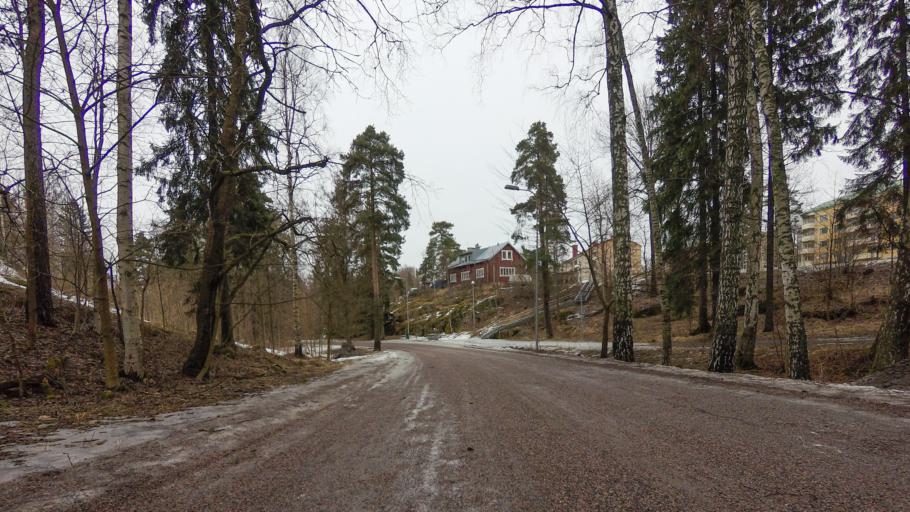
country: FI
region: Uusimaa
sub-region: Helsinki
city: Vantaa
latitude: 60.2029
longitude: 25.0313
